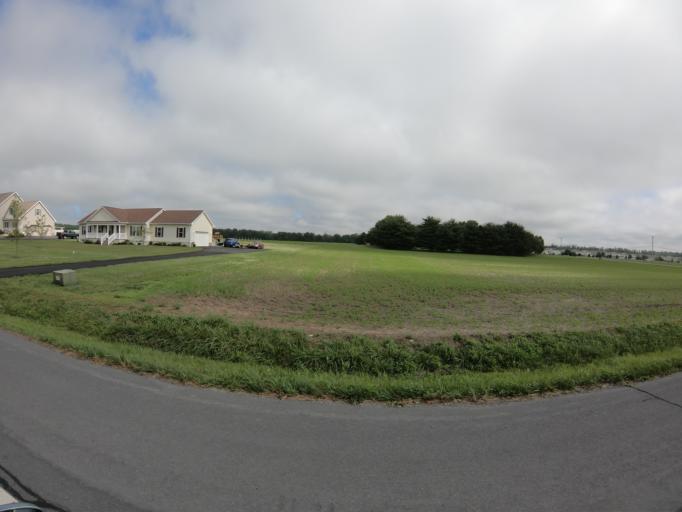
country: US
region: Delaware
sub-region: Kent County
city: Felton
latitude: 39.0068
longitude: -75.5559
